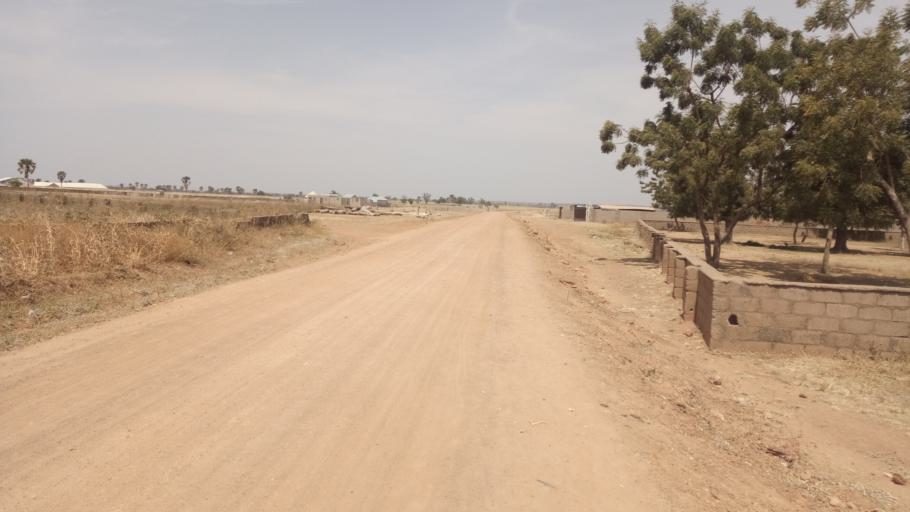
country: NG
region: Adamawa
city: Yola
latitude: 9.1176
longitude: 12.8761
